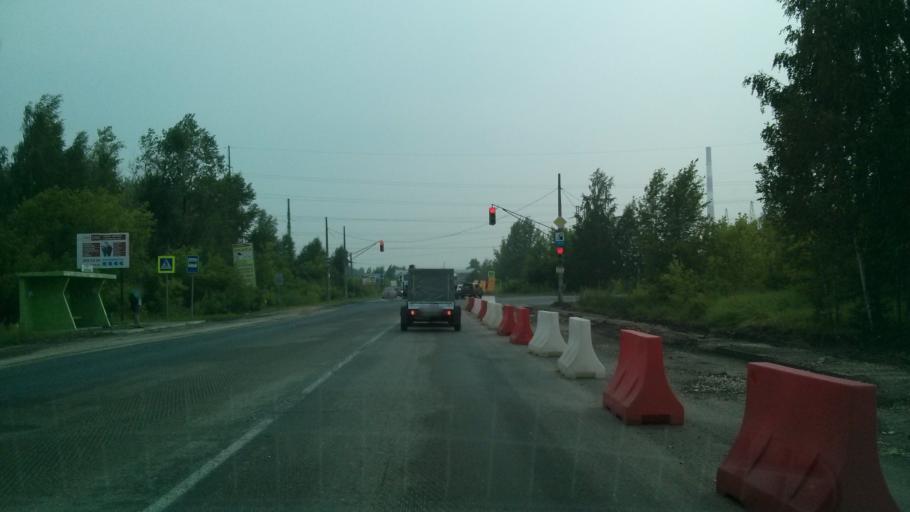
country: RU
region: Nizjnij Novgorod
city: Kstovo
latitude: 56.1176
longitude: 44.1530
